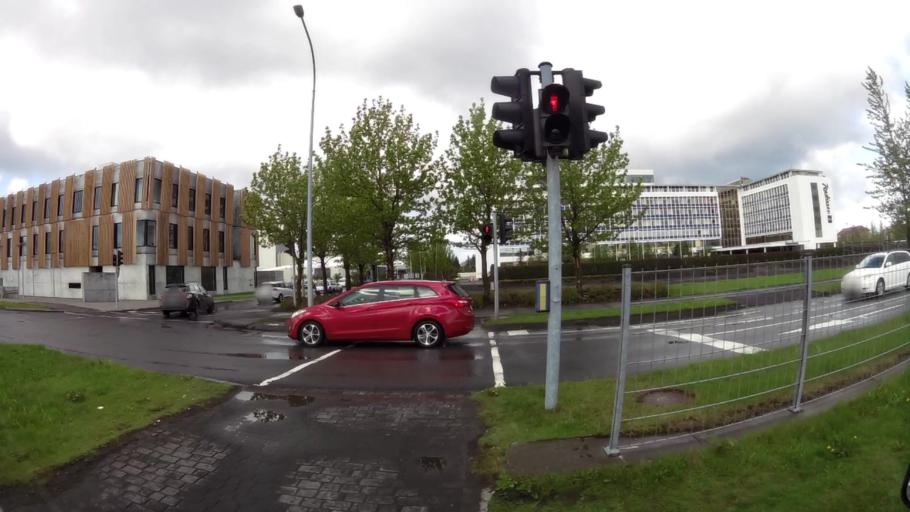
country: IS
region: Capital Region
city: Seltjarnarnes
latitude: 64.1403
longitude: -21.9511
